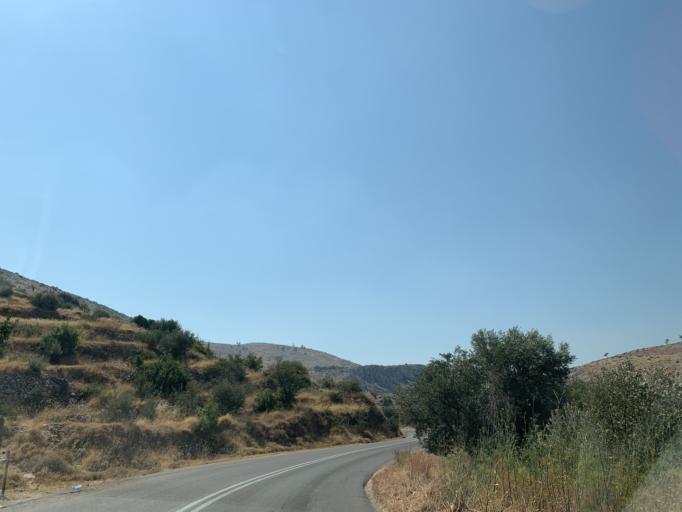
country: GR
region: North Aegean
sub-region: Chios
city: Thymiana
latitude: 38.3243
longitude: 26.0038
